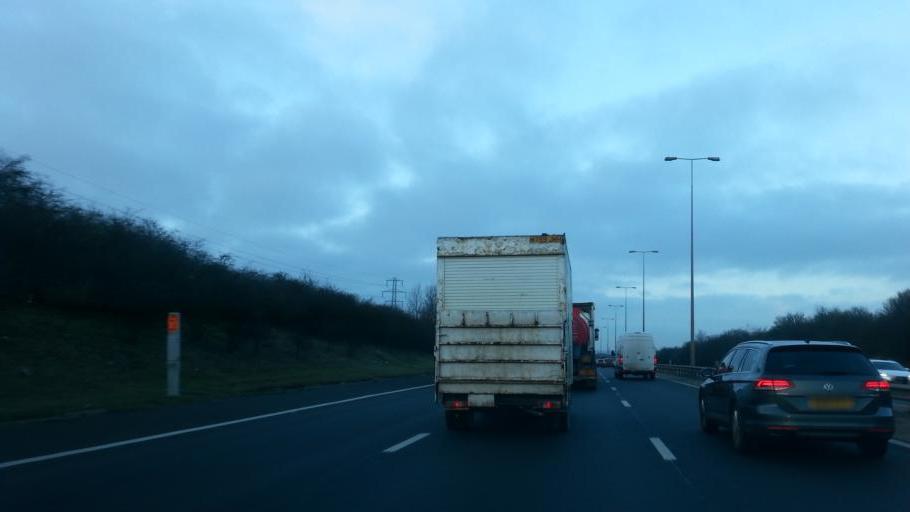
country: GB
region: England
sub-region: Worcestershire
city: Fernhill Heath
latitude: 52.1900
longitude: -2.1690
